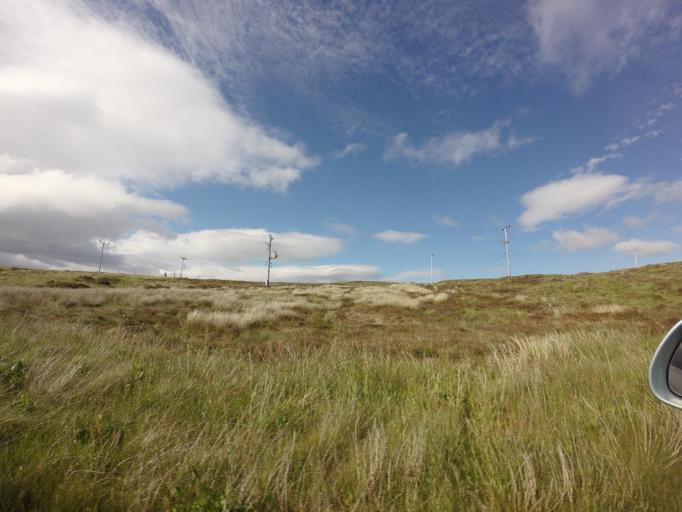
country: GB
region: Scotland
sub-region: Eilean Siar
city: Stornoway
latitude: 58.1766
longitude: -6.6186
